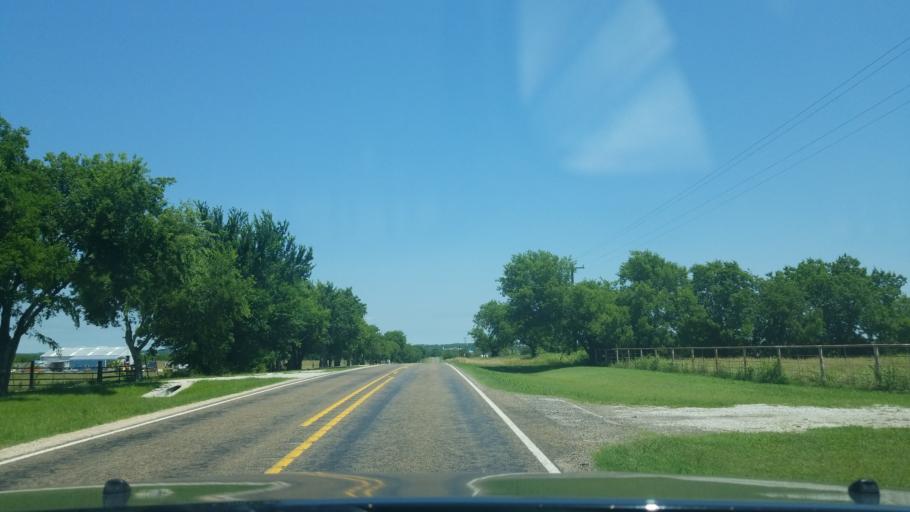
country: US
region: Texas
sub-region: Denton County
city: Sanger
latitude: 33.3368
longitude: -97.2385
